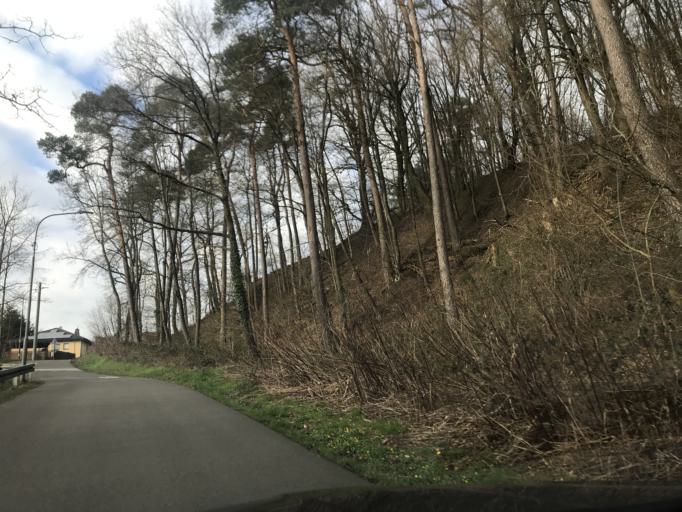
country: DE
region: Saarland
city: Blieskastel
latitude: 49.2562
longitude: 7.2536
